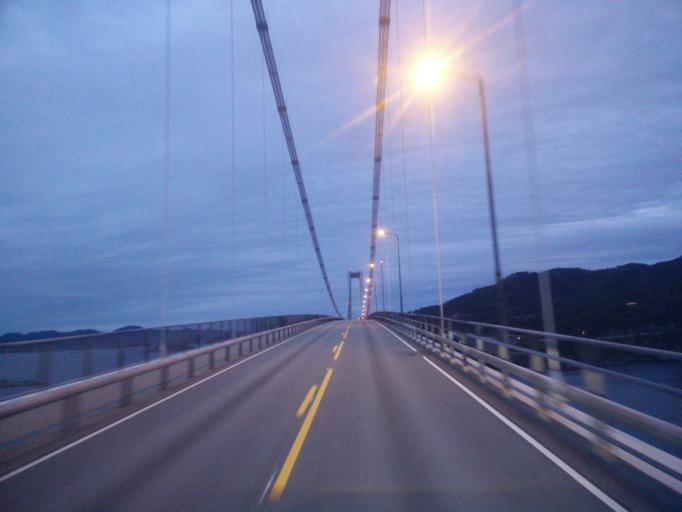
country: NO
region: More og Romsdal
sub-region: Gjemnes
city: Batnfjordsora
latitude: 62.9695
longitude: 7.7764
